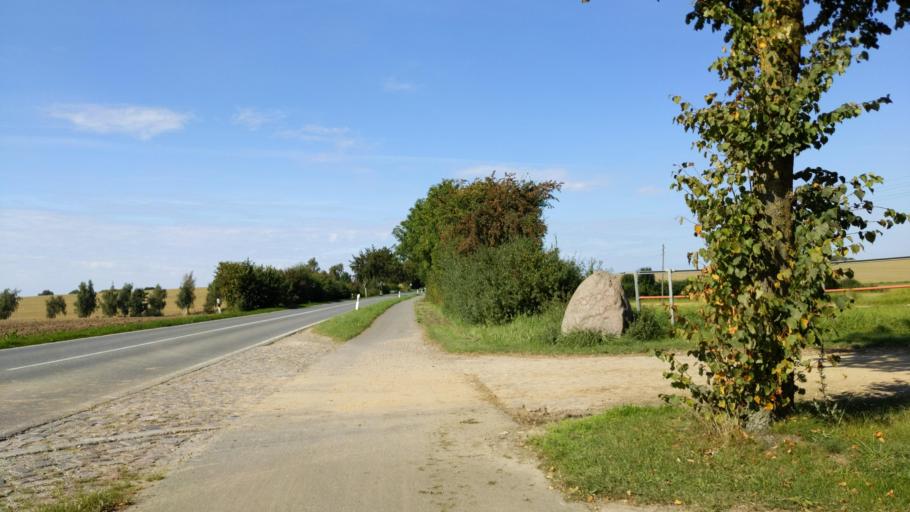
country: DE
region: Schleswig-Holstein
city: Stockelsdorf
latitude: 53.9290
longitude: 10.6352
